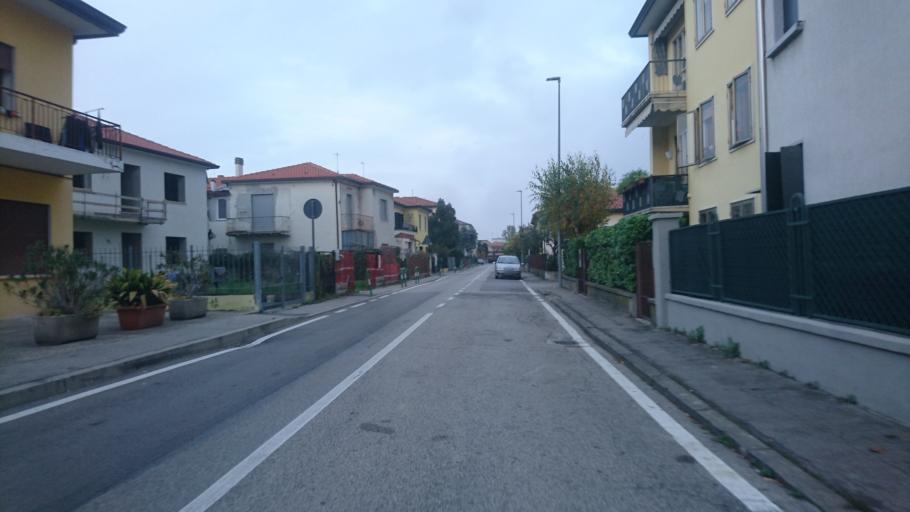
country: IT
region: Veneto
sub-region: Provincia di Padova
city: Padova
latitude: 45.4258
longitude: 11.8742
